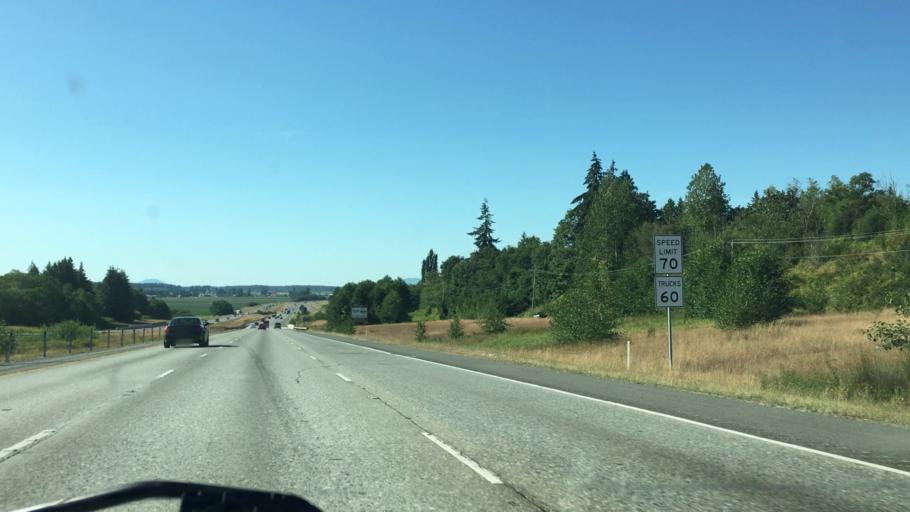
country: US
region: Washington
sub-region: Snohomish County
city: Stanwood
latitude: 48.3166
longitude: -122.3240
